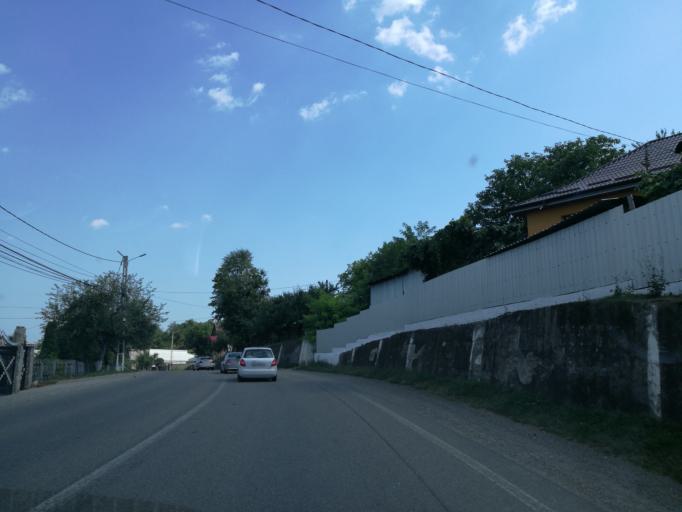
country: RO
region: Neamt
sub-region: Comuna Baltatesti
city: Baltatesti
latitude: 47.1266
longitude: 26.3129
